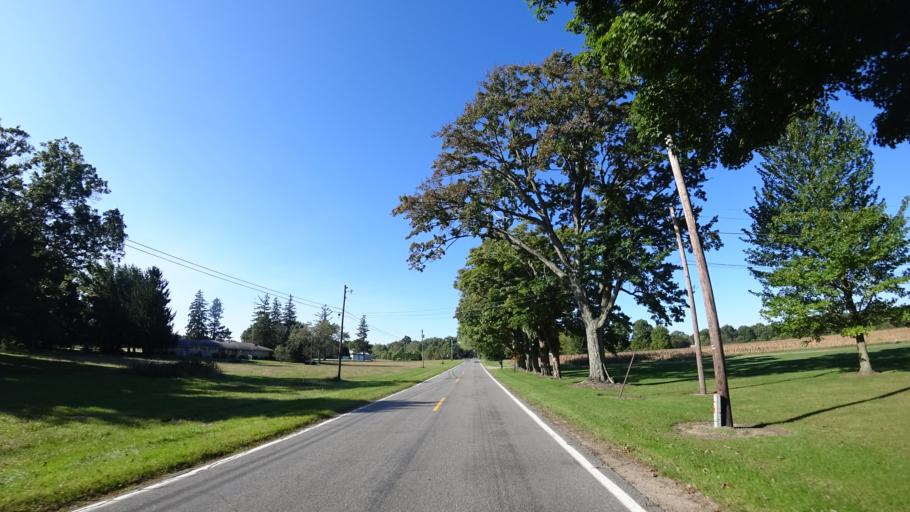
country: US
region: Michigan
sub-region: Berrien County
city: Benton Heights
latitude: 42.1659
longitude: -86.4006
